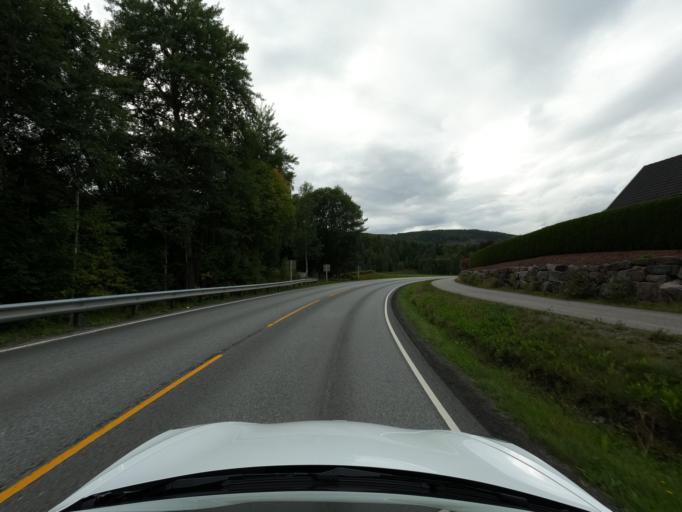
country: NO
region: Telemark
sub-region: Sauherad
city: Gvarv
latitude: 59.3809
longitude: 9.1717
